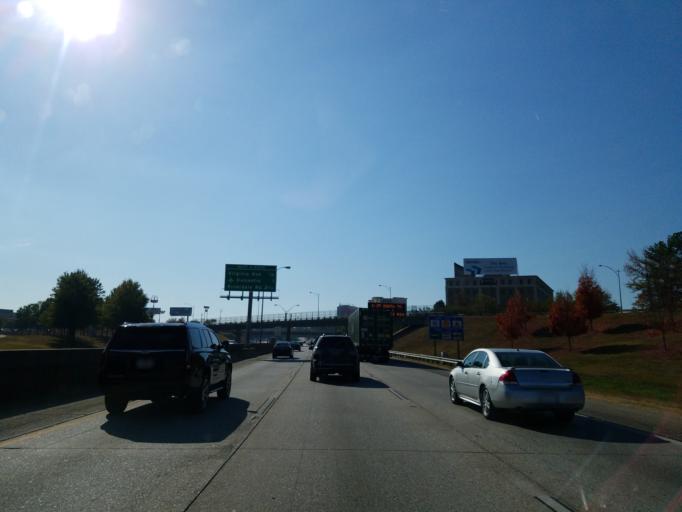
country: US
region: Georgia
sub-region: Fulton County
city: Hapeville
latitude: 33.6626
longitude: -84.4253
